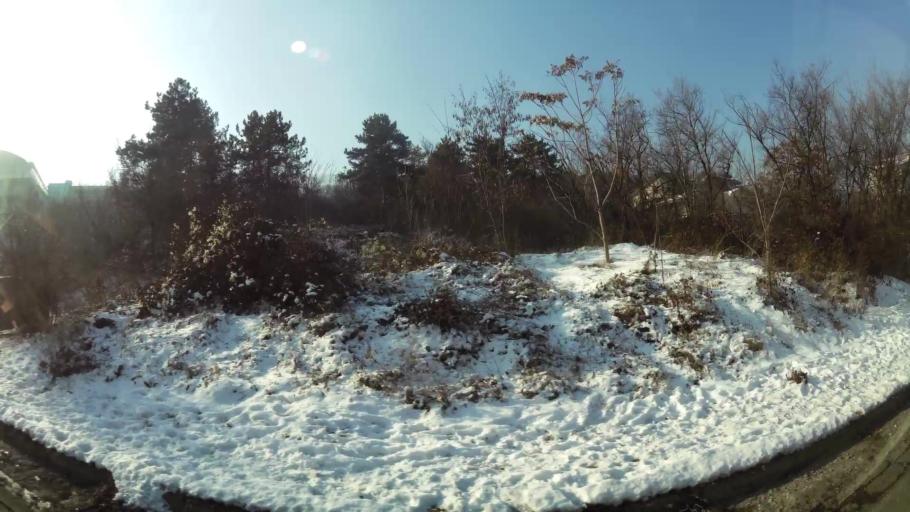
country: MK
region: Karpos
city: Skopje
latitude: 41.9827
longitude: 21.4216
